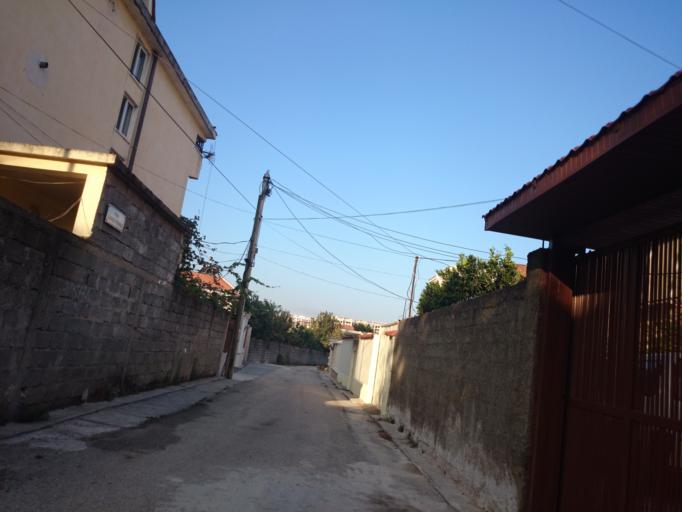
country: AL
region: Tirane
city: Tirana
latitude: 41.3280
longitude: 19.7929
